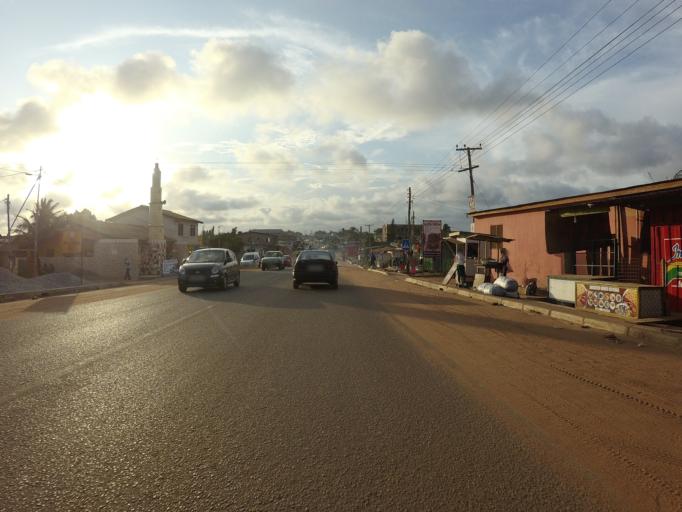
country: GH
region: Greater Accra
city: Teshi Old Town
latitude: 5.5953
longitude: -0.1224
